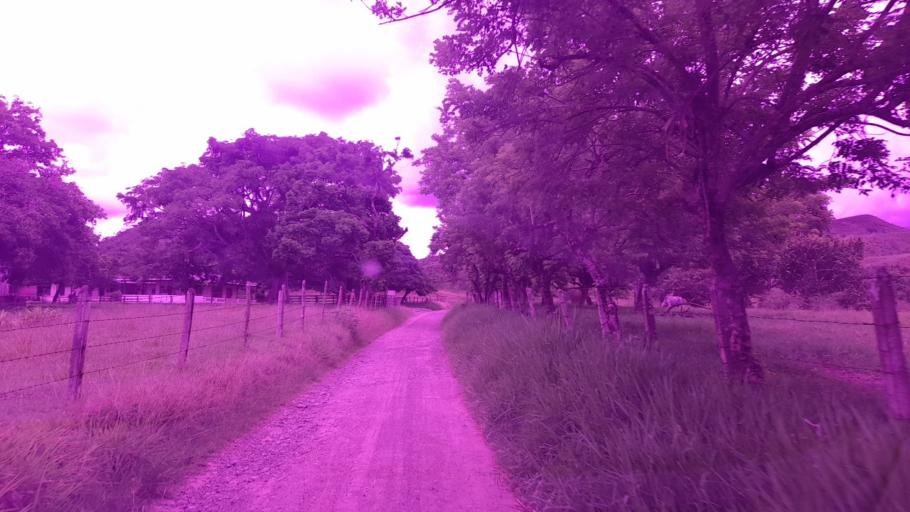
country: CO
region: Valle del Cauca
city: Andalucia
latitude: 4.1764
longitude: -76.1281
